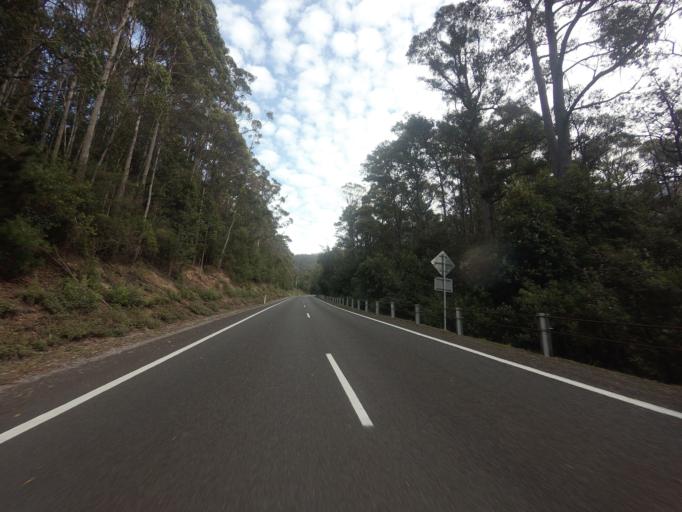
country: AU
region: Tasmania
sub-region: Meander Valley
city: Deloraine
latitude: -41.6490
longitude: 146.7189
